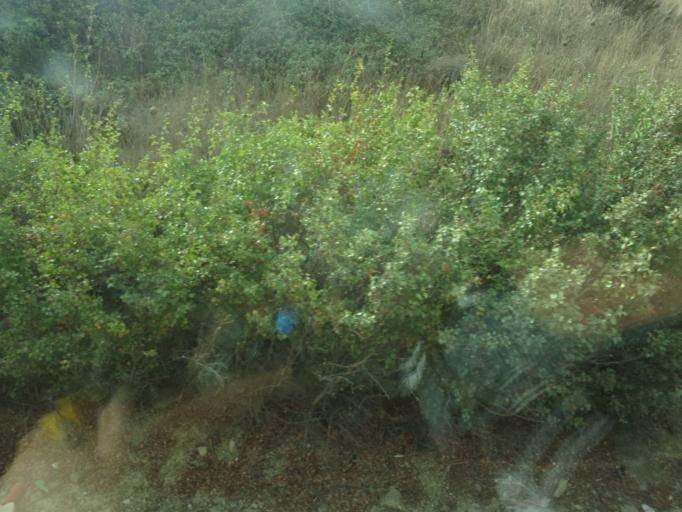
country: ES
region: Andalusia
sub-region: Provincia de Cadiz
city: Tarifa
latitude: 36.0237
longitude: -5.5947
